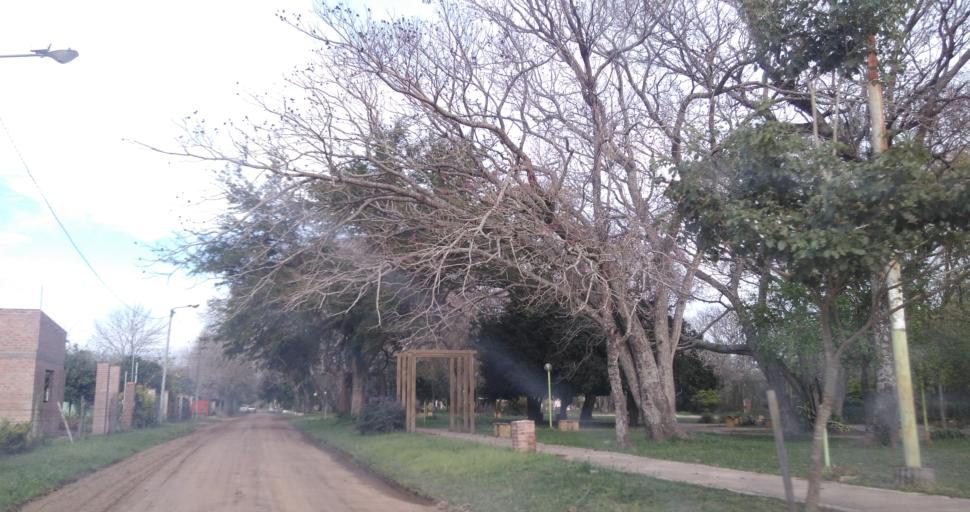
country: AR
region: Chaco
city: Colonia Benitez
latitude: -27.3296
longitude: -58.9551
